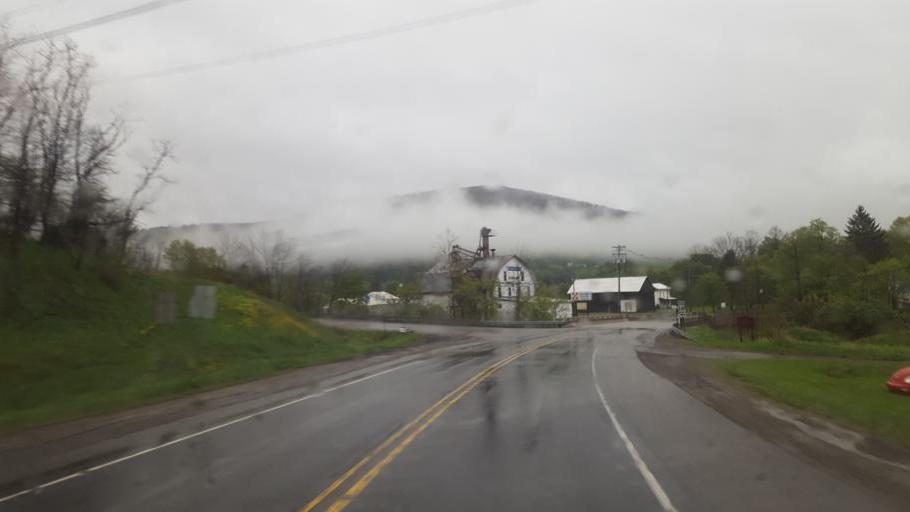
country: US
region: Pennsylvania
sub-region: Tioga County
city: Westfield
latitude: 41.9573
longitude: -77.4452
